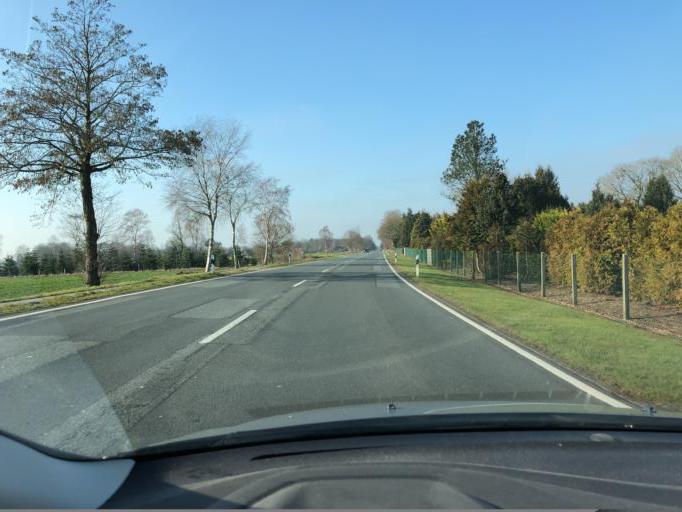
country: DE
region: Lower Saxony
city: Schwerinsdorf
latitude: 53.2991
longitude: 7.7243
